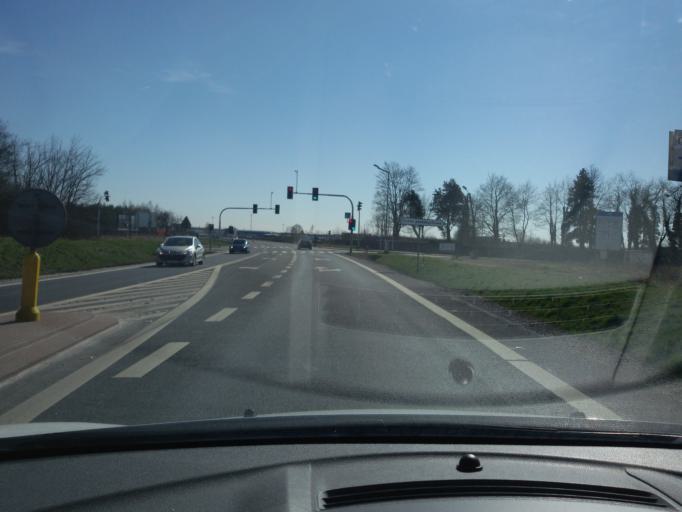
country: PL
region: Greater Poland Voivodeship
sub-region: Powiat leszczynski
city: Rydzyna
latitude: 51.7909
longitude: 16.6520
